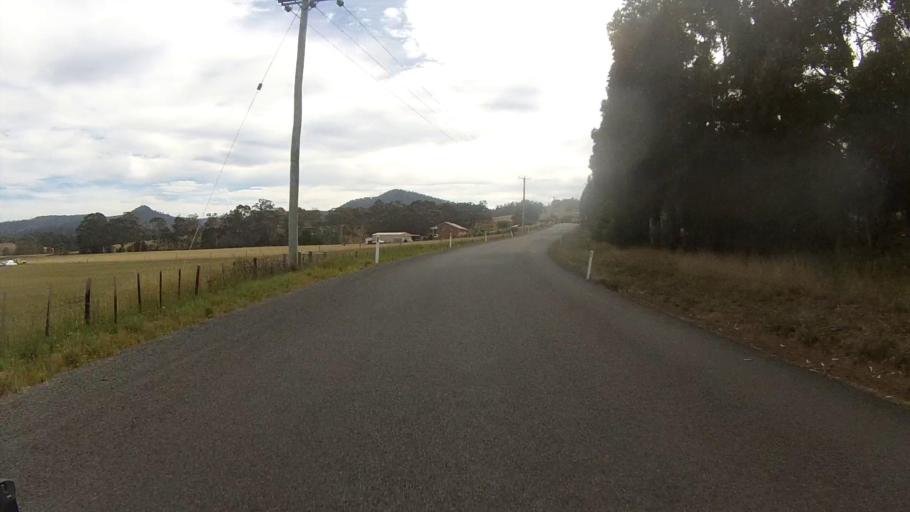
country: AU
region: Tasmania
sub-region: Sorell
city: Sorell
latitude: -42.7907
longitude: 147.8005
